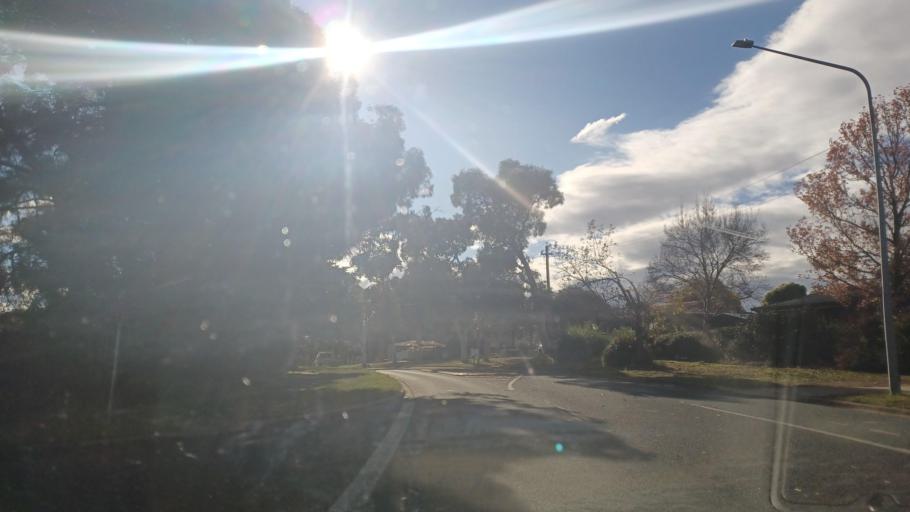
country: AU
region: Australian Capital Territory
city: Belconnen
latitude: -35.1981
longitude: 149.0445
